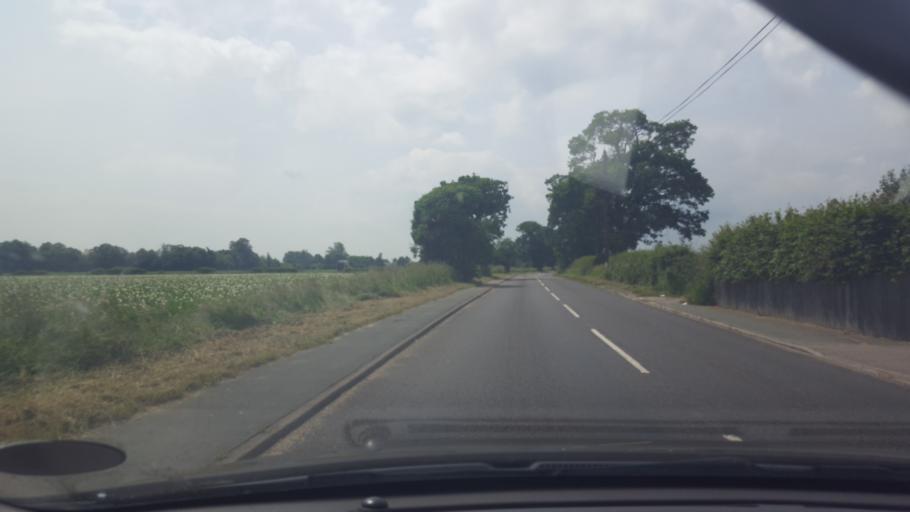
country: GB
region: England
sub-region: Essex
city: Great Bentley
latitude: 51.8806
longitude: 1.1163
